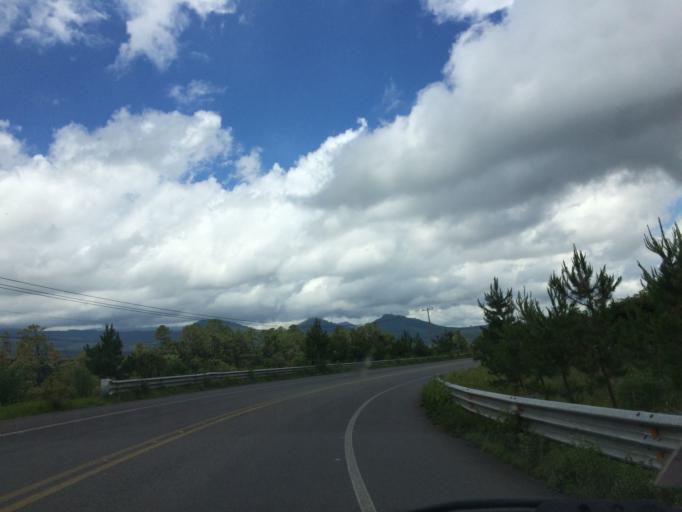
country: MX
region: Michoacan
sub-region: Uruapan
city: Santa Ana Zirosto
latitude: 19.5524
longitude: -102.3004
